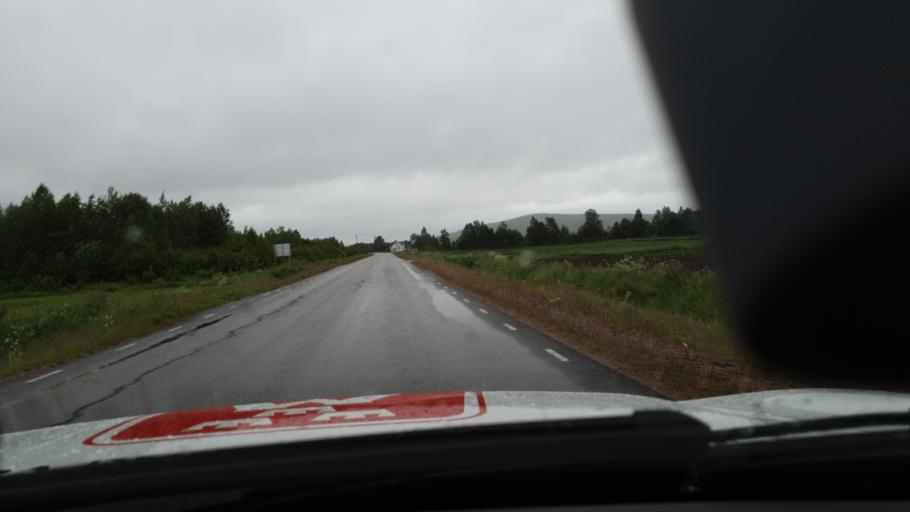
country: SE
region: Norrbotten
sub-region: Overtornea Kommun
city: OEvertornea
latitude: 66.5536
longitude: 23.8122
